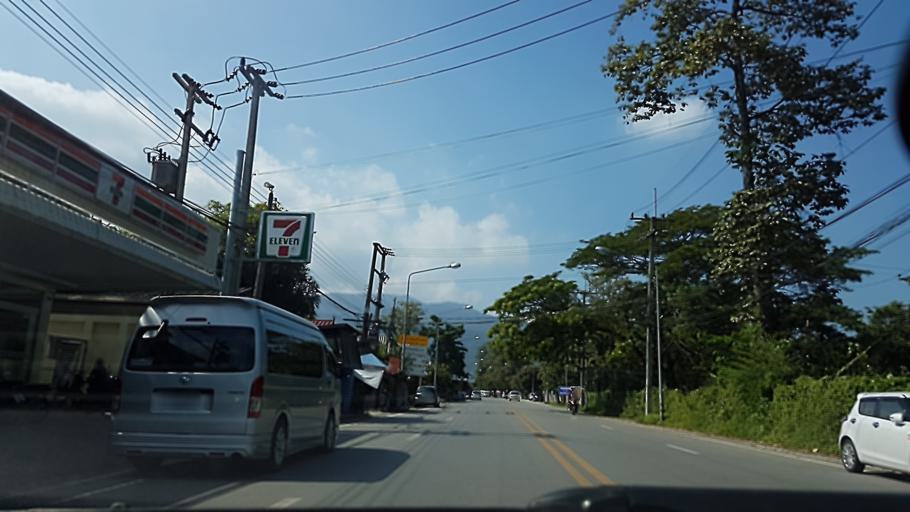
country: TH
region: Chiang Mai
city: Chiang Mai
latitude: 18.8194
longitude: 98.9733
